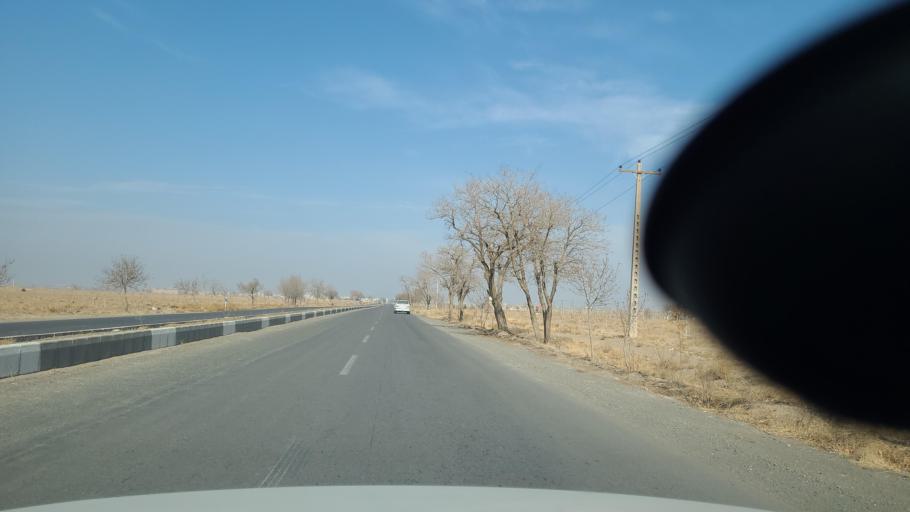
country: IR
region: Razavi Khorasan
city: Fariman
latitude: 35.6658
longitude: 59.8417
